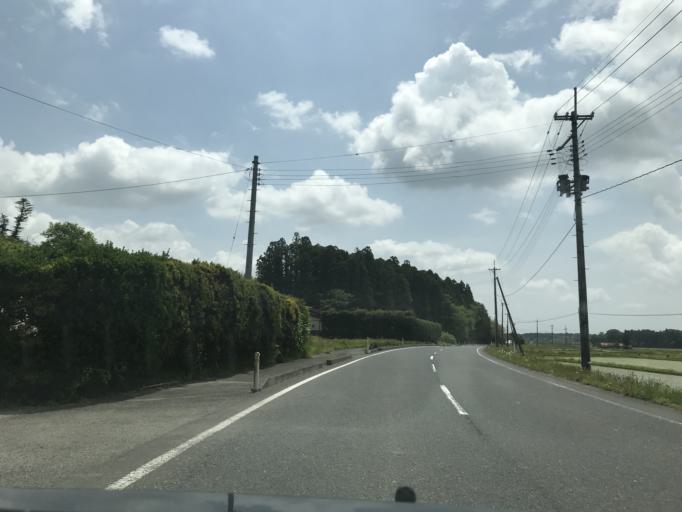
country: JP
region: Miyagi
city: Furukawa
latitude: 38.6853
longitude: 140.9733
